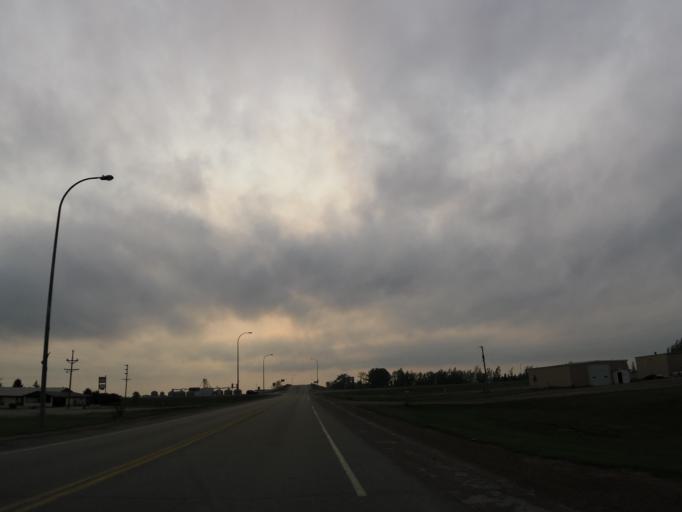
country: US
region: North Dakota
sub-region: Walsh County
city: Grafton
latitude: 48.5713
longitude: -97.1823
